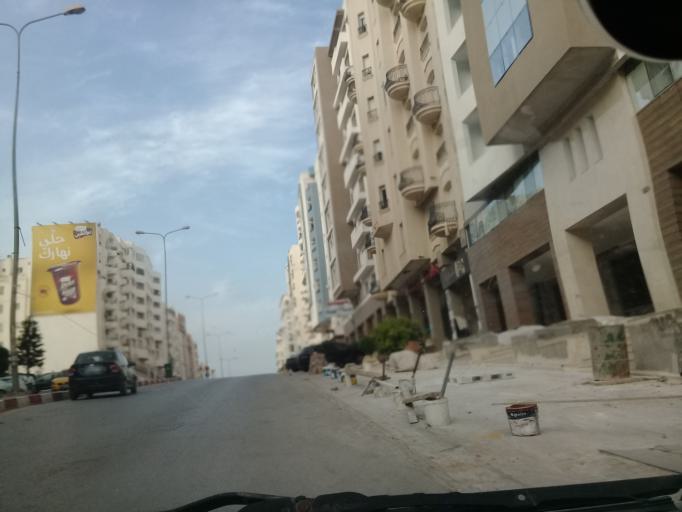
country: TN
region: Ariana
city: Ariana
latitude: 36.8621
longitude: 10.1649
